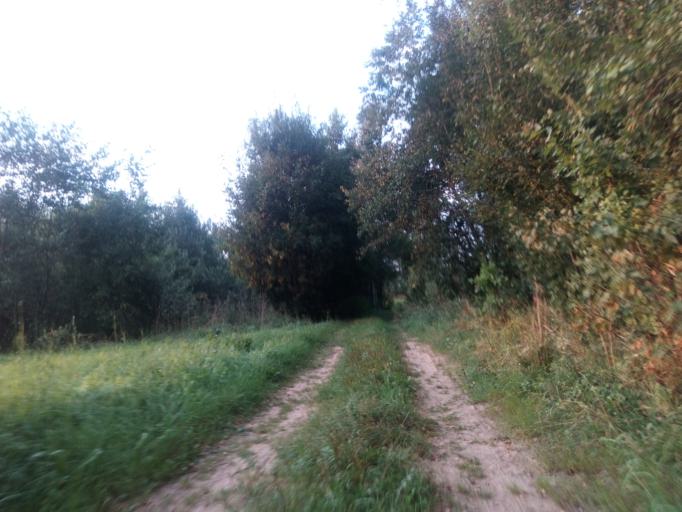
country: BY
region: Vitebsk
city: Dzisna
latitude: 55.6581
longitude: 28.3304
